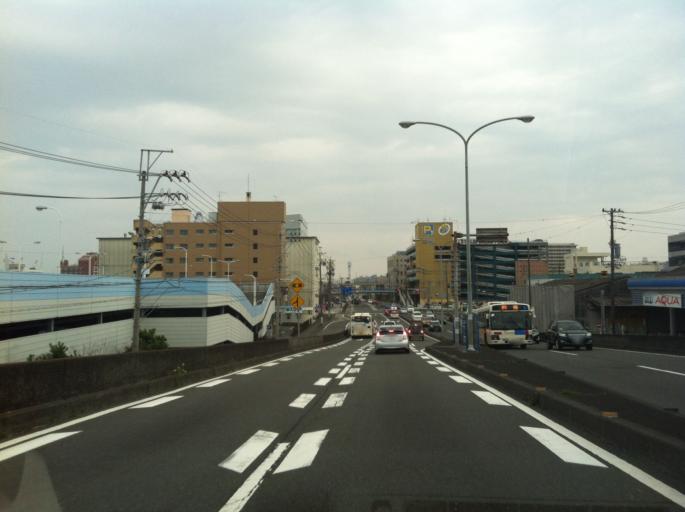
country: JP
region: Shizuoka
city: Shizuoka-shi
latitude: 35.0131
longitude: 138.4915
